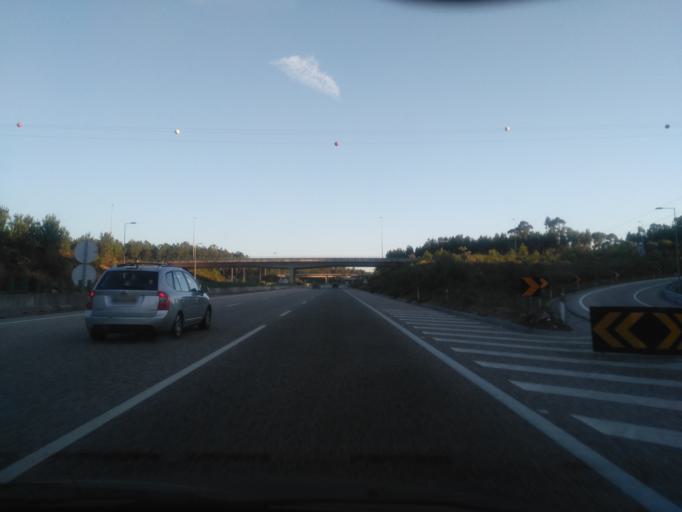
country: PT
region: Leiria
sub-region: Pombal
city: Lourical
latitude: 39.9457
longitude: -8.7707
